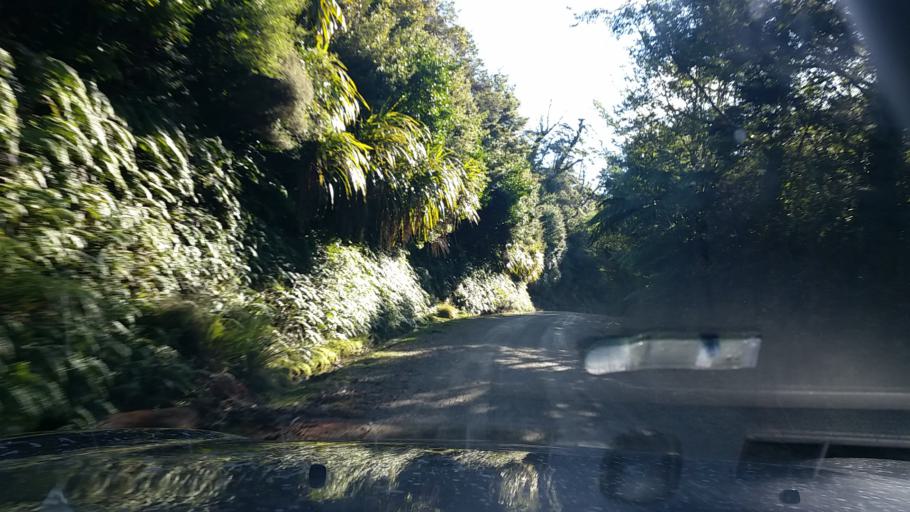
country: NZ
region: Marlborough
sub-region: Marlborough District
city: Picton
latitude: -41.0607
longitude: 174.1604
